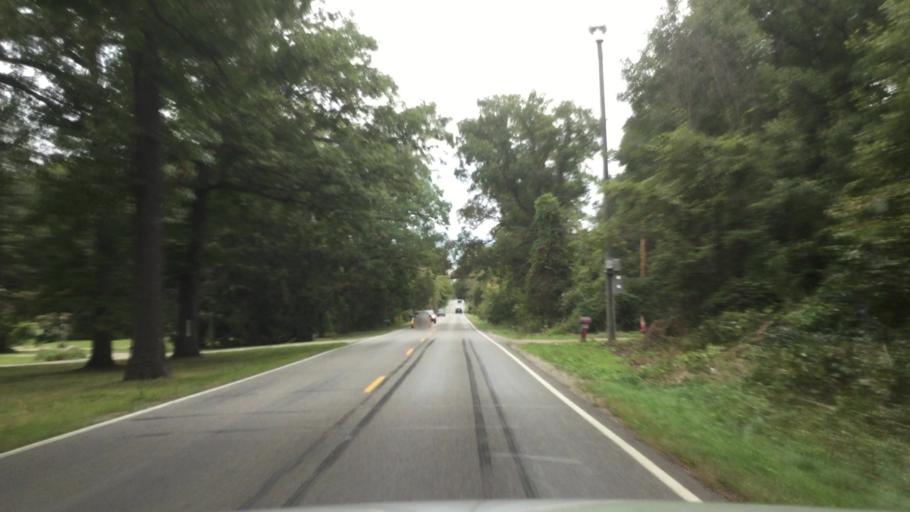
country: US
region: Michigan
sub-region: Livingston County
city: Whitmore Lake
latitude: 42.4757
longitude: -83.7670
